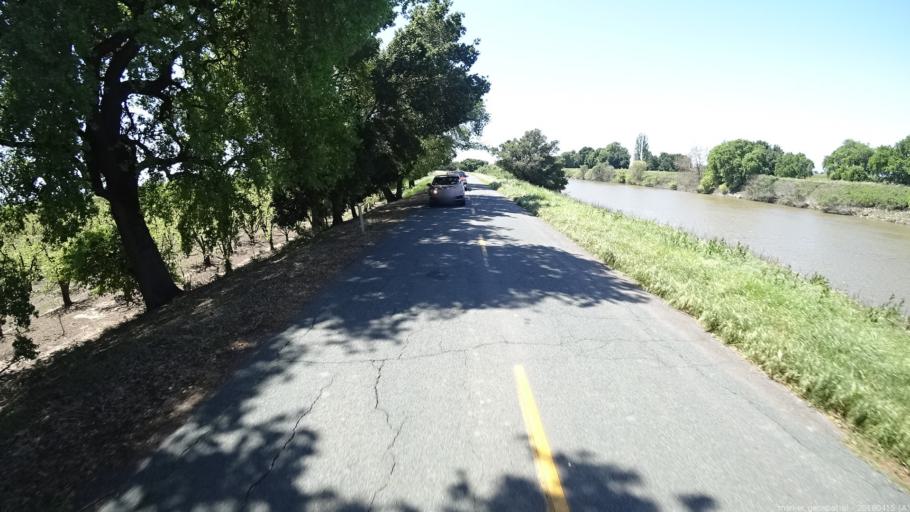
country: US
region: California
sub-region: Sacramento County
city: Walnut Grove
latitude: 38.2861
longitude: -121.5843
